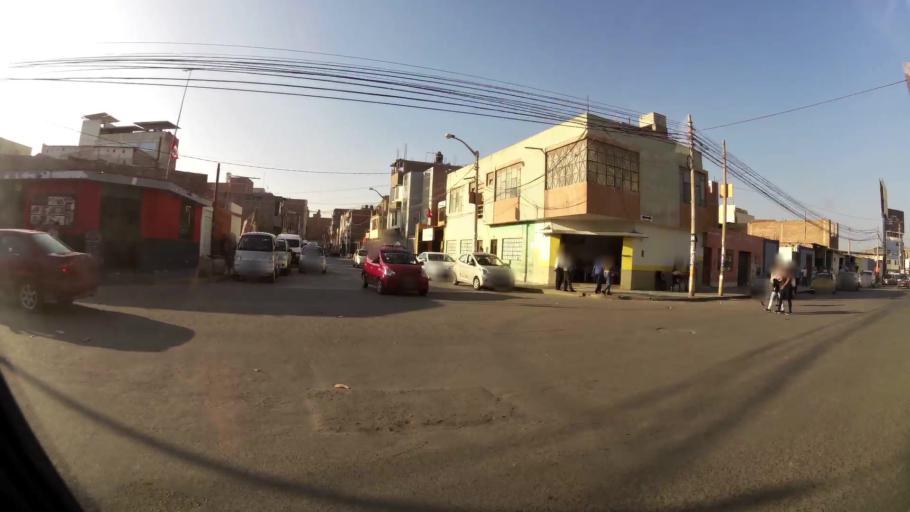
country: PE
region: Lambayeque
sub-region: Provincia de Chiclayo
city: Chiclayo
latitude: -6.7759
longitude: -79.8367
